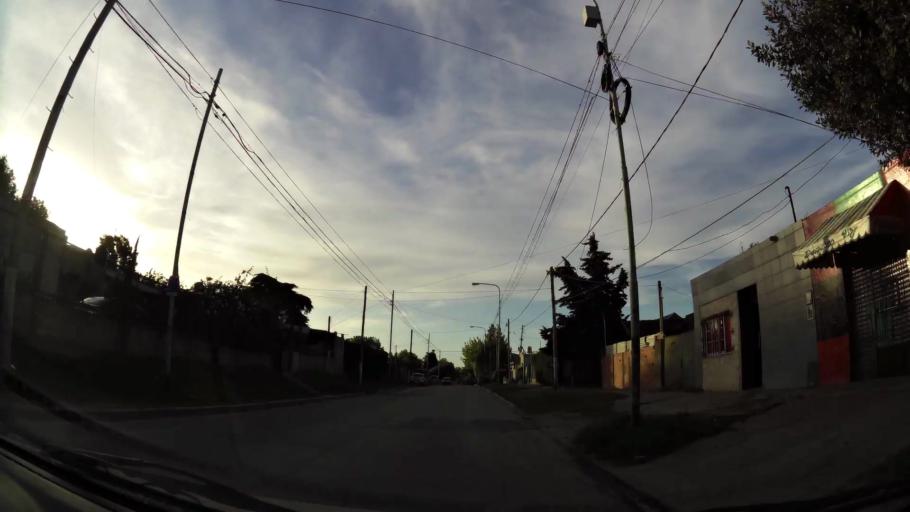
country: AR
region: Buenos Aires
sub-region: Partido de Quilmes
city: Quilmes
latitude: -34.7831
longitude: -58.1899
